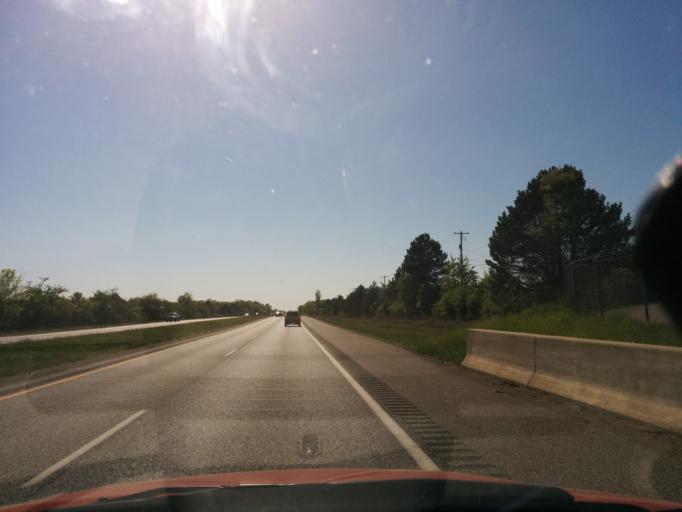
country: US
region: Michigan
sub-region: Midland County
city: Midland
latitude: 43.6561
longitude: -84.2276
